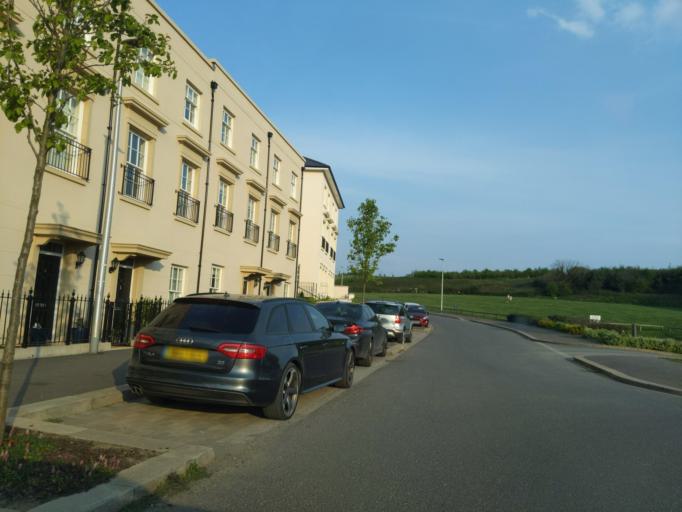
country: GB
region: England
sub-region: Devon
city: Plympton
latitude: 50.3628
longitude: -4.0507
